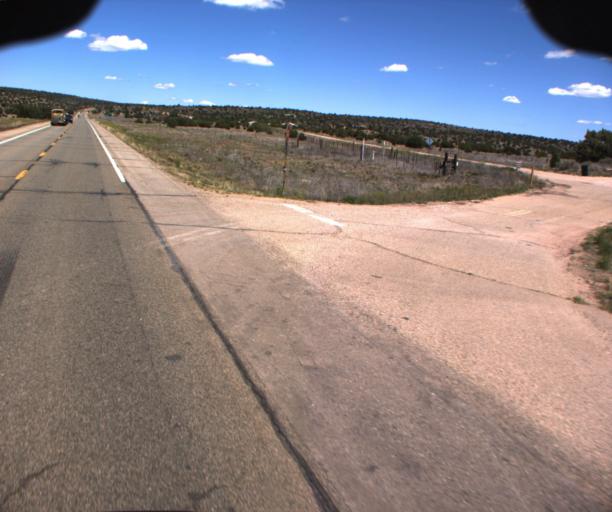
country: US
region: Arizona
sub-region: Yavapai County
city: Paulden
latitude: 34.9143
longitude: -112.4578
